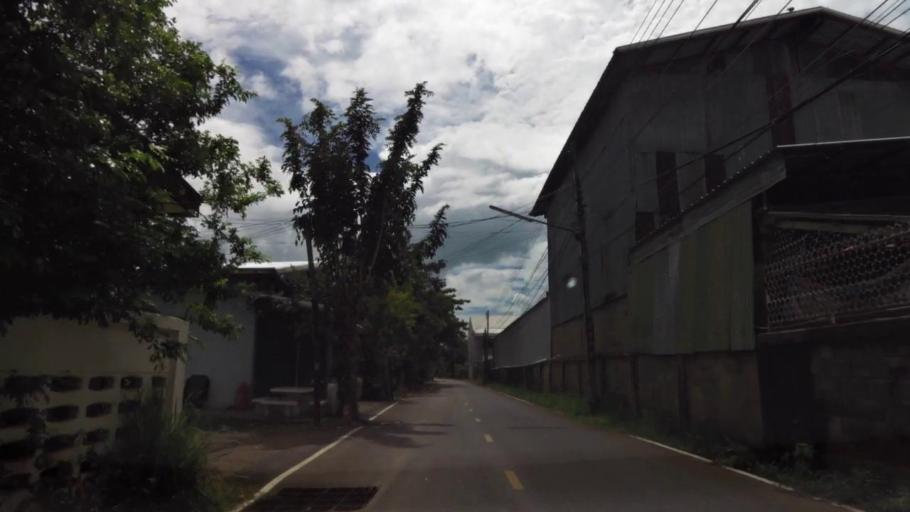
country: TH
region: Nakhon Sawan
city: Phai Sali
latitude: 15.5956
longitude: 100.6451
